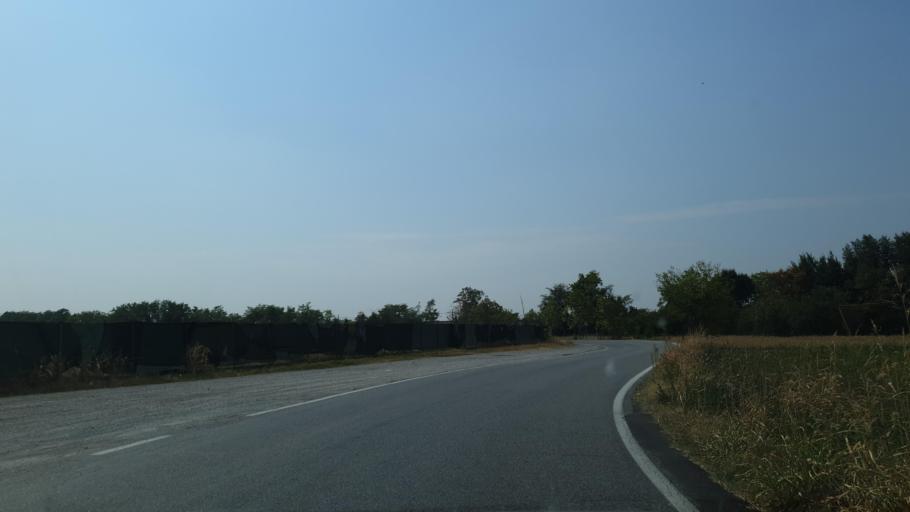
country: IT
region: Lombardy
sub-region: Provincia di Brescia
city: Montirone
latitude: 45.4429
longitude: 10.2529
